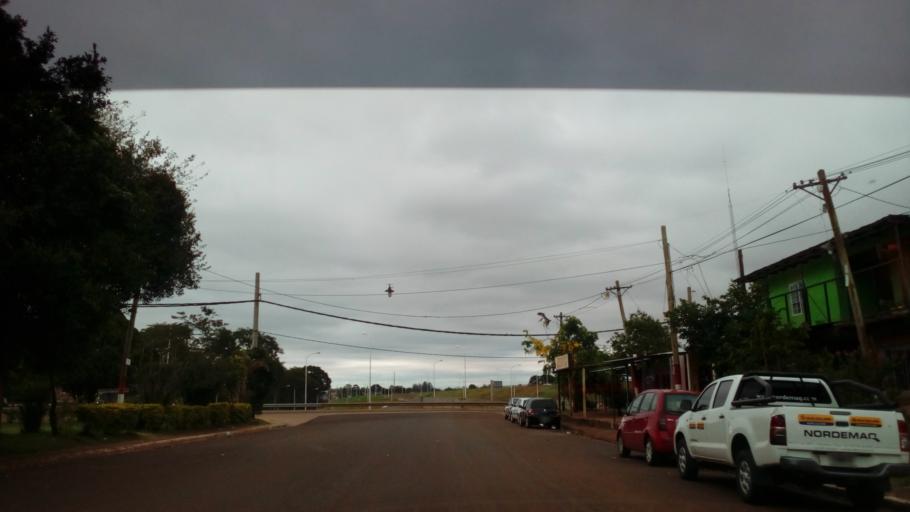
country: AR
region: Misiones
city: Garupa
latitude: -27.4564
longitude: -55.8619
